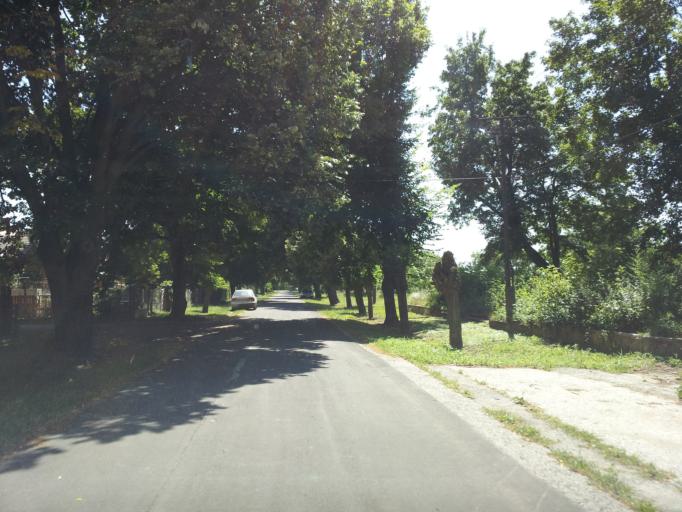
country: HU
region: Veszprem
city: Berhida
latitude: 47.1149
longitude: 18.1046
